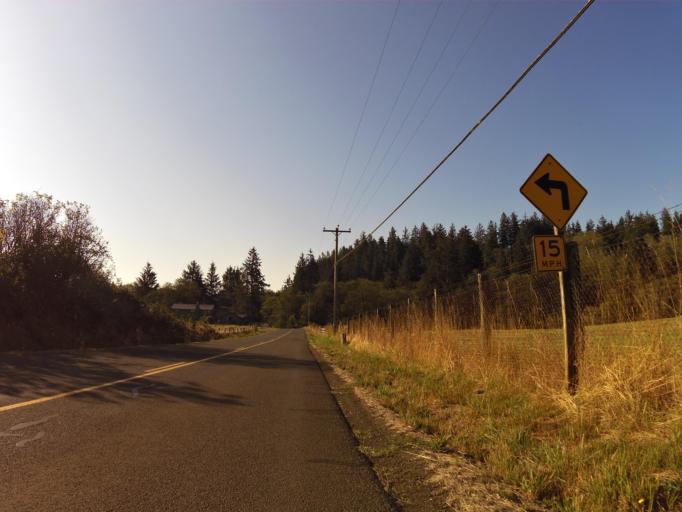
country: US
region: Oregon
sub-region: Tillamook County
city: Tillamook
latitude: 45.4218
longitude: -123.7829
